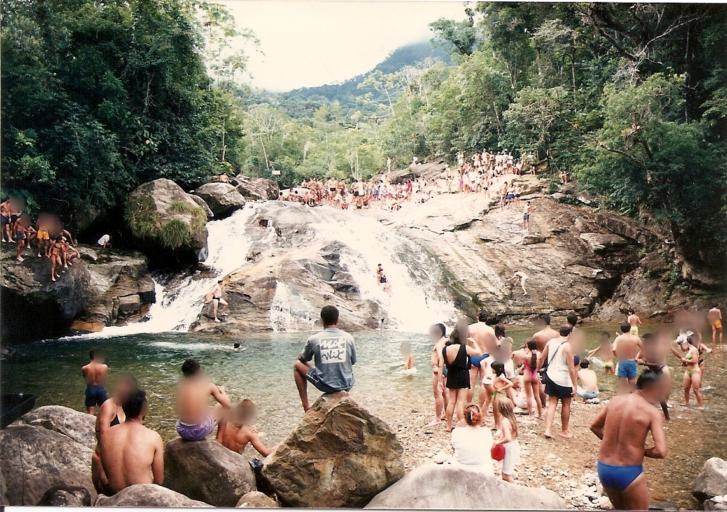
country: BR
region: Sao Paulo
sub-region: Peruibe
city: Peruibe
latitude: -24.3950
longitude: -47.1223
